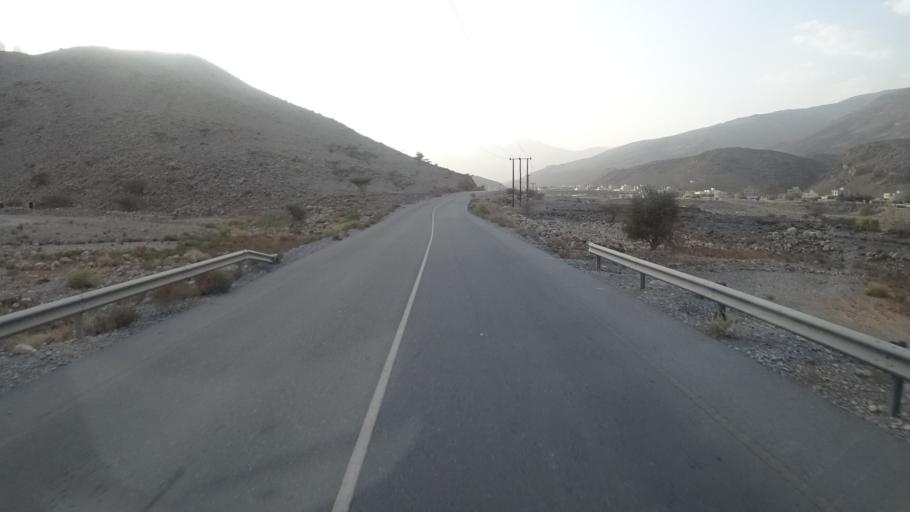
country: OM
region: Muhafazat ad Dakhiliyah
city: Bahla'
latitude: 23.1410
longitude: 57.2205
